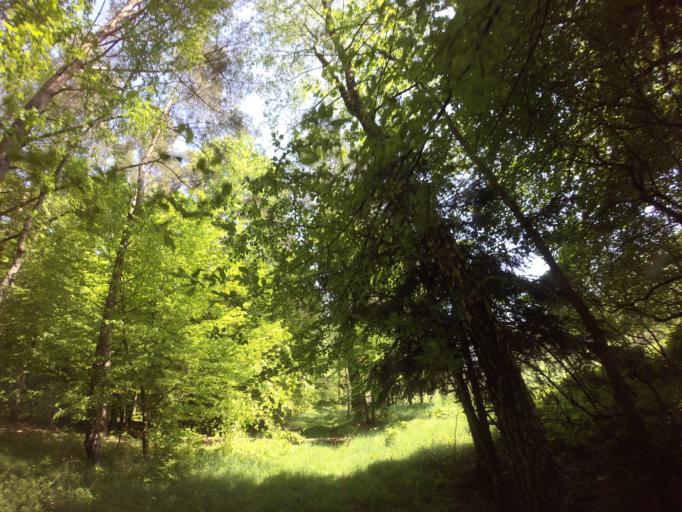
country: PL
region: West Pomeranian Voivodeship
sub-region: Powiat choszczenski
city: Pelczyce
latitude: 52.9508
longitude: 15.3269
